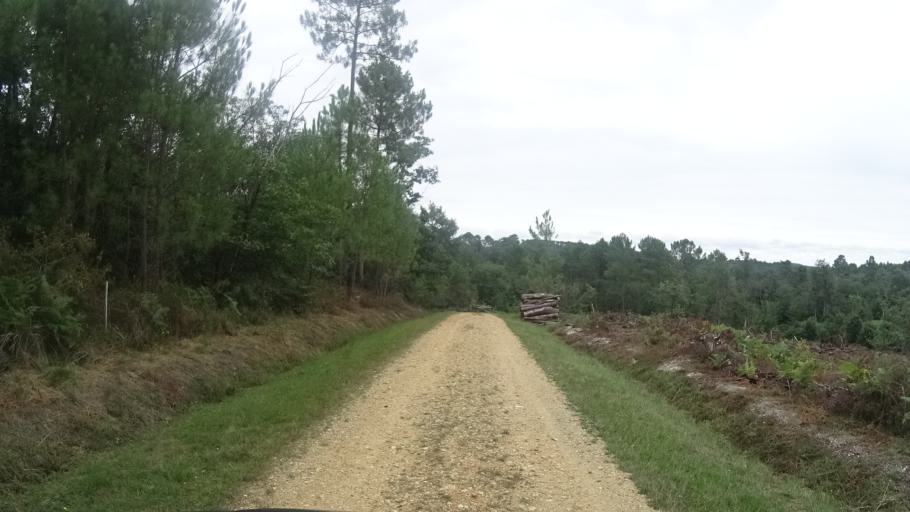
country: FR
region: Aquitaine
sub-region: Departement de la Dordogne
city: Sourzac
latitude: 45.0322
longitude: 0.4141
